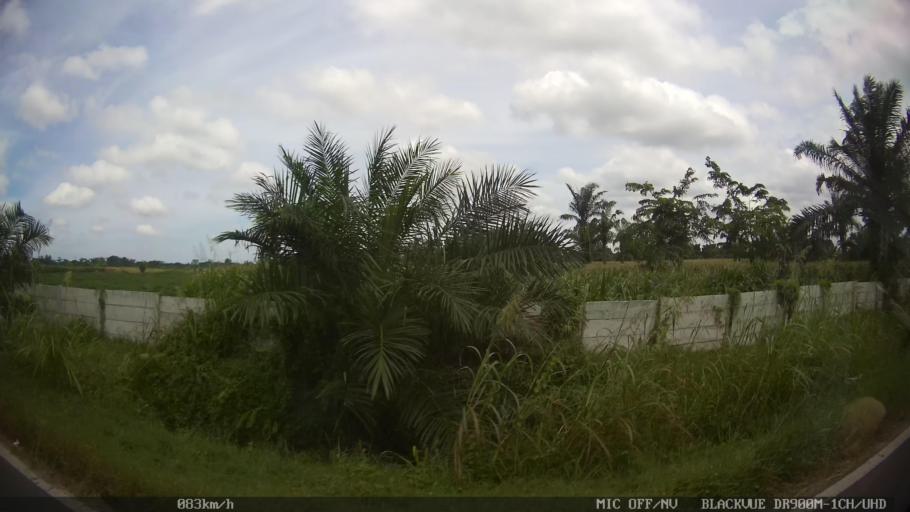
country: ID
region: North Sumatra
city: Percut
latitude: 3.6009
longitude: 98.8387
